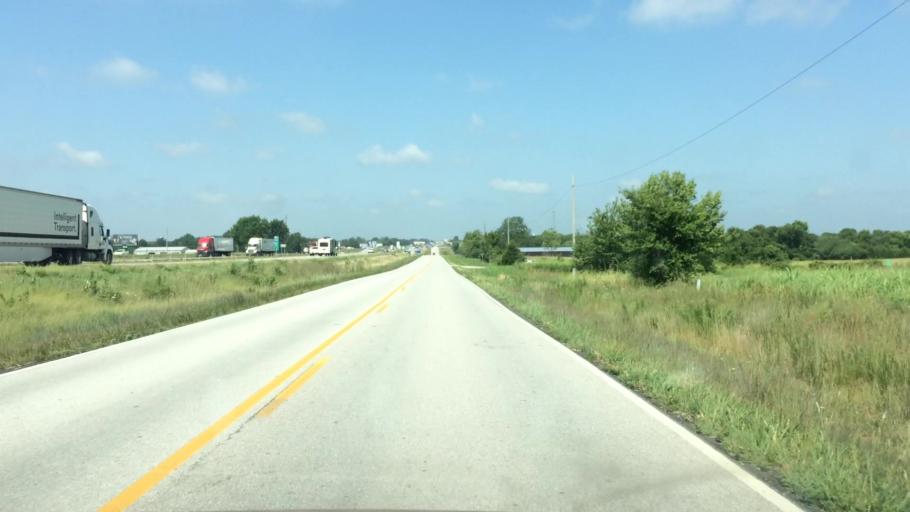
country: US
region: Missouri
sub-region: Greene County
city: Strafford
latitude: 37.2708
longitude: -93.0719
